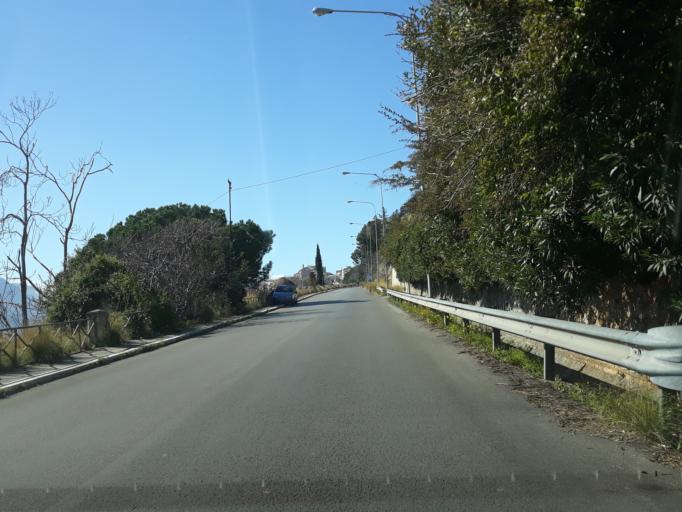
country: IT
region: Sicily
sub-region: Palermo
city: Monreale
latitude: 38.0898
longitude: 13.3008
